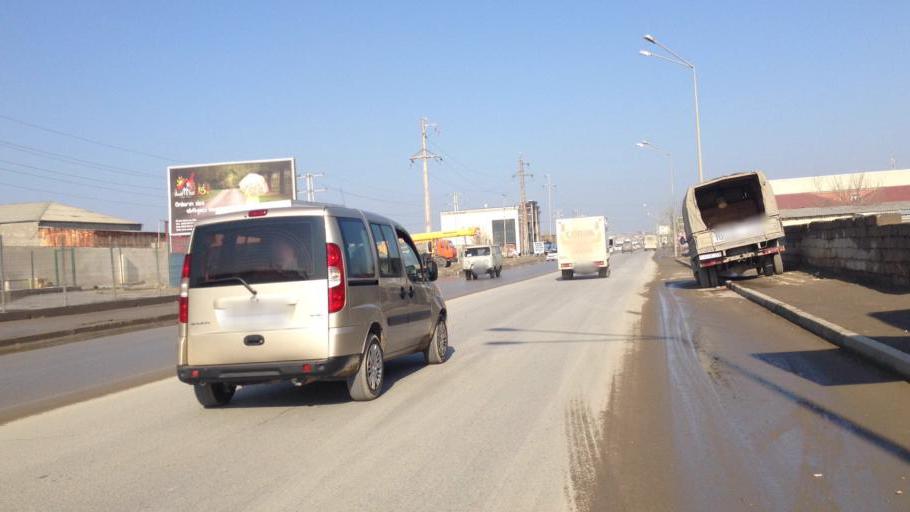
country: AZ
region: Baki
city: Binagadi
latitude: 40.4460
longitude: 49.8441
